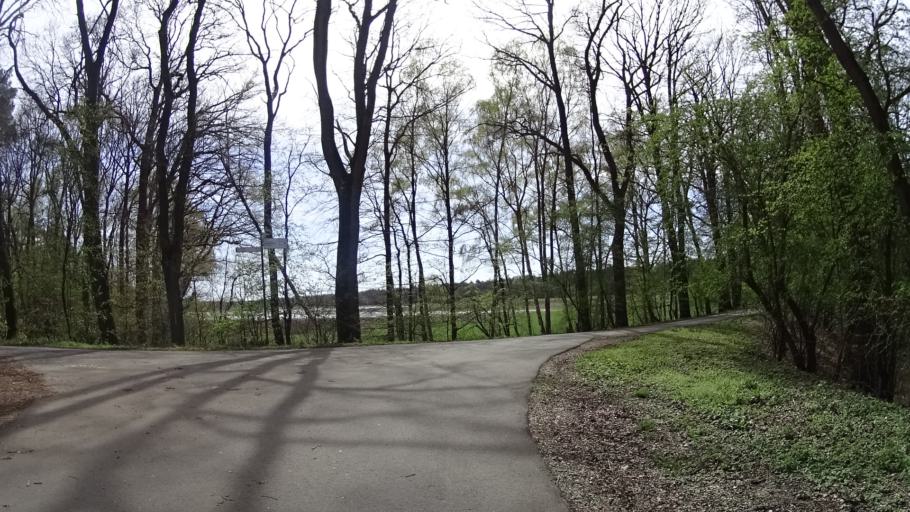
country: DE
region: Lower Saxony
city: Lunne
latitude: 52.4043
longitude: 7.3766
